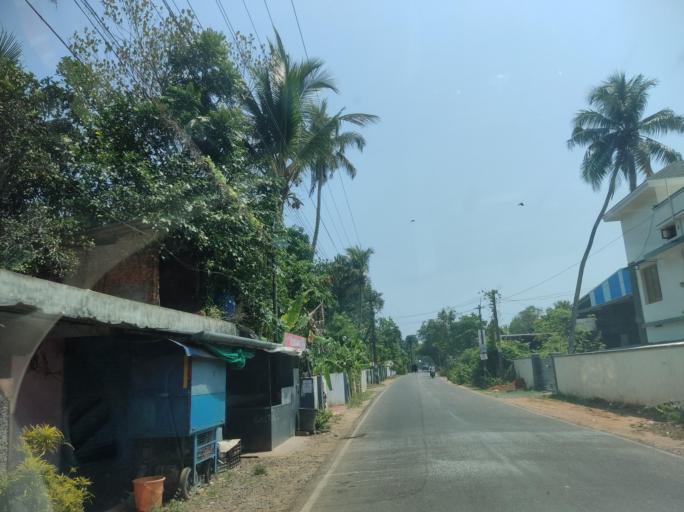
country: IN
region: Kerala
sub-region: Alappuzha
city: Kutiatodu
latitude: 9.8123
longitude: 76.3004
